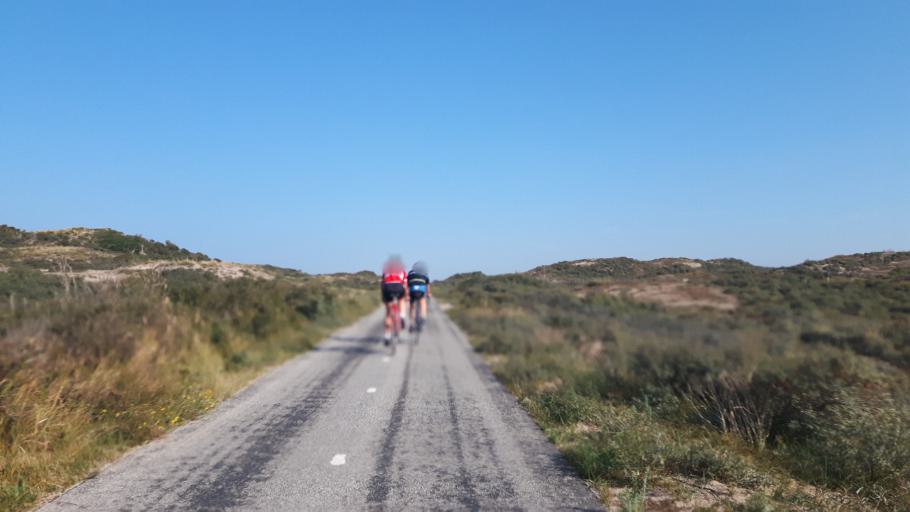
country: NL
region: North Holland
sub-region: Gemeente Zandvoort
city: Zandvoort
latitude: 52.3295
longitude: 4.4988
